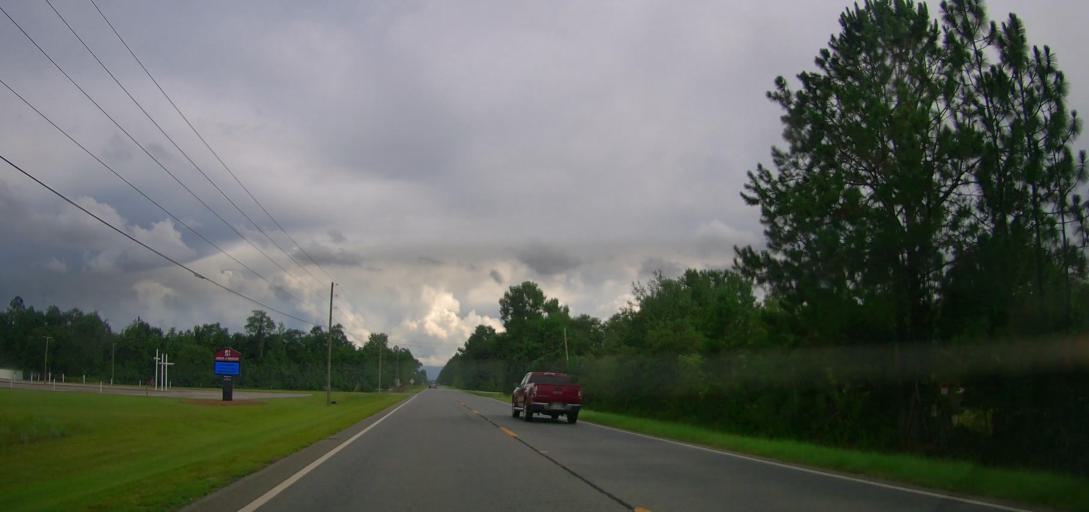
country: US
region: Georgia
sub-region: Wayne County
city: Jesup
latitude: 31.6428
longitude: -81.9064
